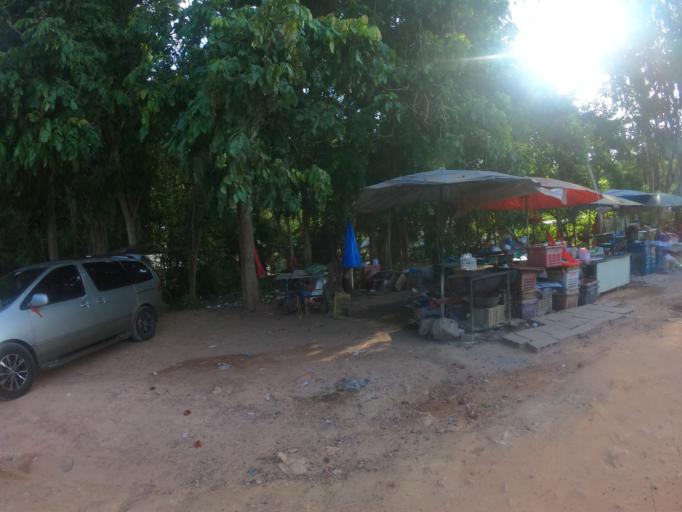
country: TH
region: Surin
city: Kap Choeng
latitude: 14.4348
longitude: 103.6995
